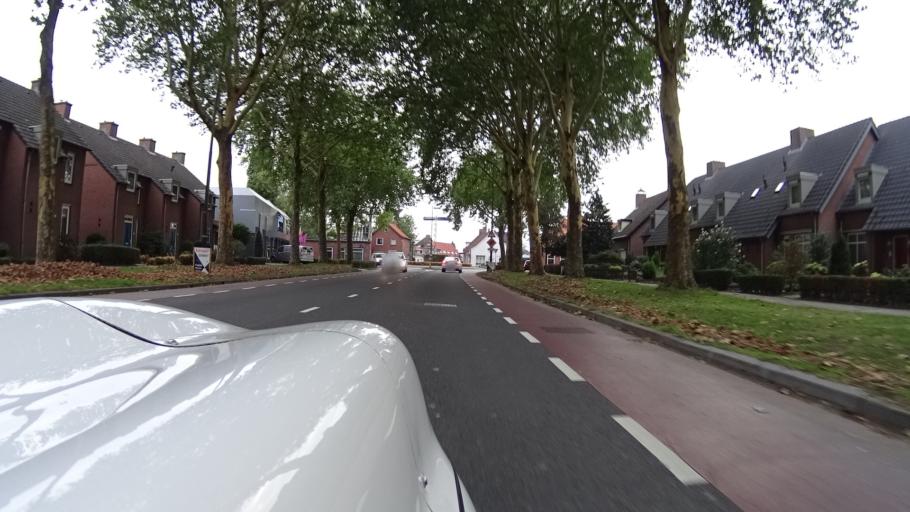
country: NL
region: North Brabant
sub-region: Gemeente Boekel
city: Boekel
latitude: 51.5596
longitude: 5.6825
